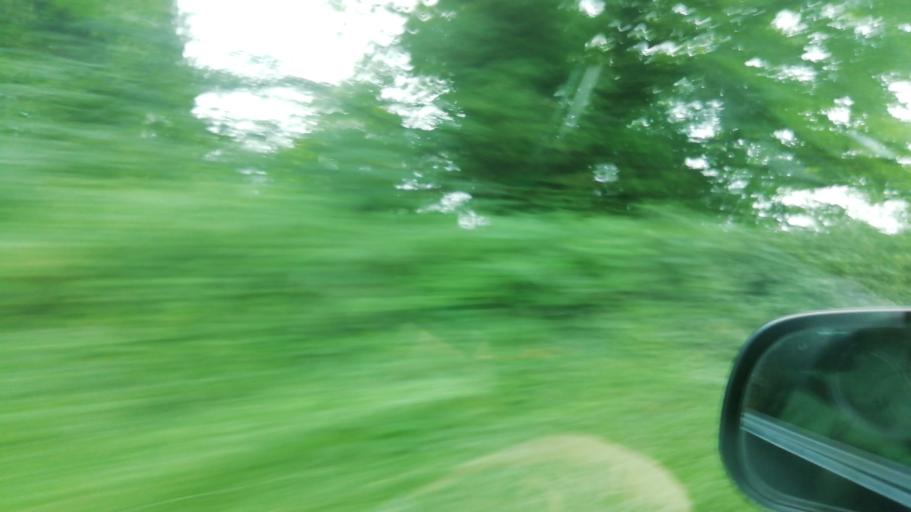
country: IE
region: Munster
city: Fethard
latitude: 52.5149
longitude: -7.6844
